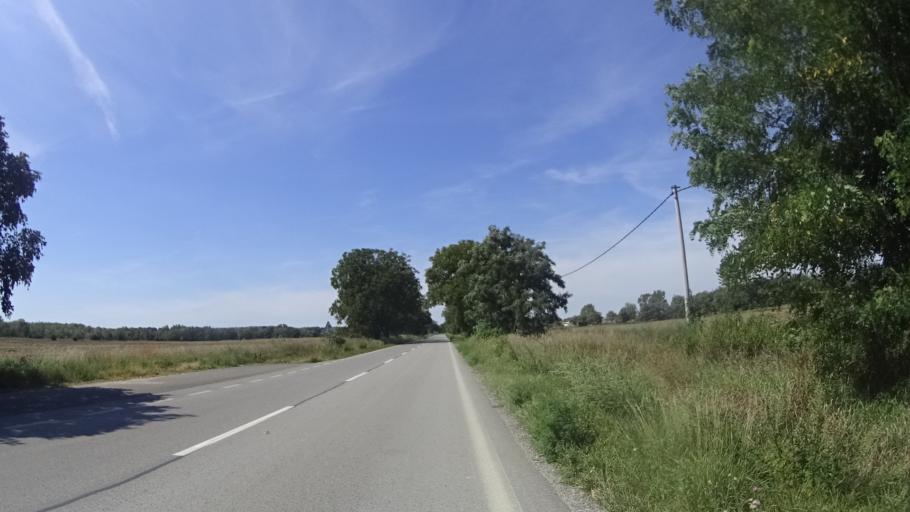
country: AT
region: Lower Austria
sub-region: Politischer Bezirk Ganserndorf
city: Marchegg
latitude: 48.3170
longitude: 16.9227
